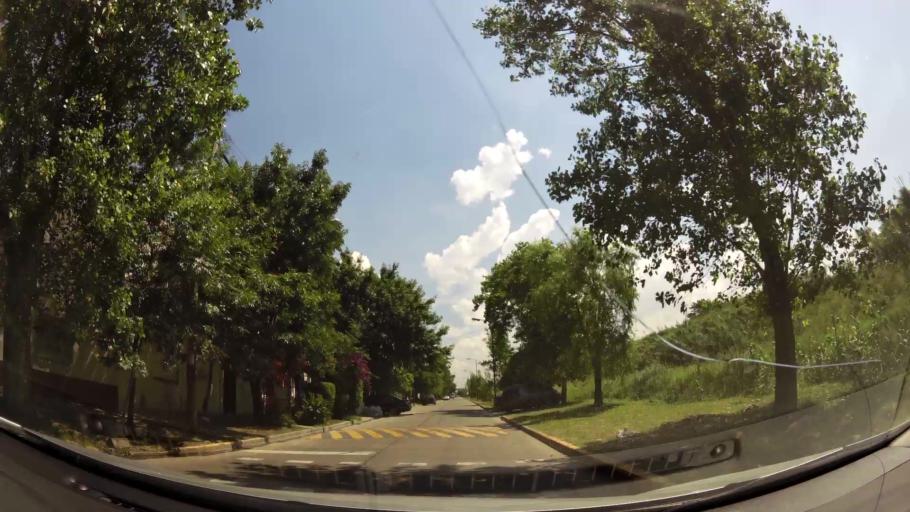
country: AR
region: Buenos Aires
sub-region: Partido de Tigre
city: Tigre
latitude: -34.4650
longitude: -58.5858
